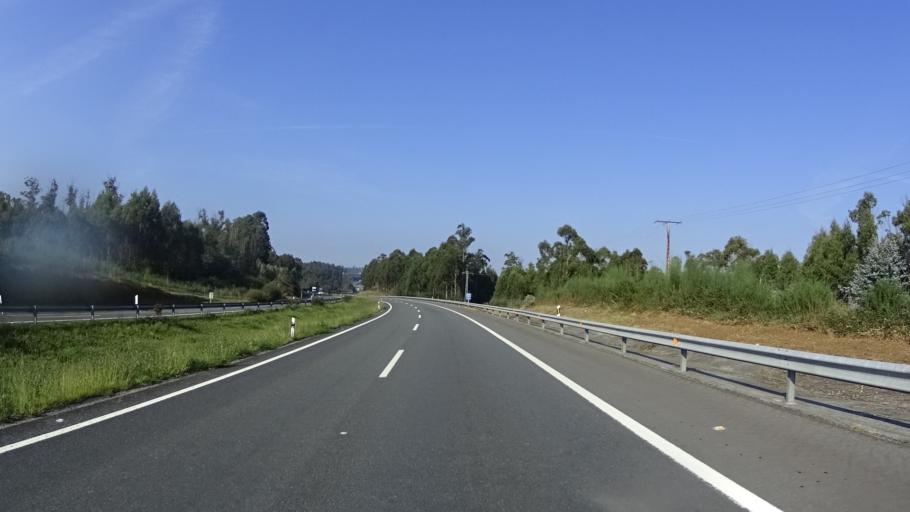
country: ES
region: Galicia
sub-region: Provincia da Coruna
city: Irixoa
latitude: 43.2426
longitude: -8.1011
